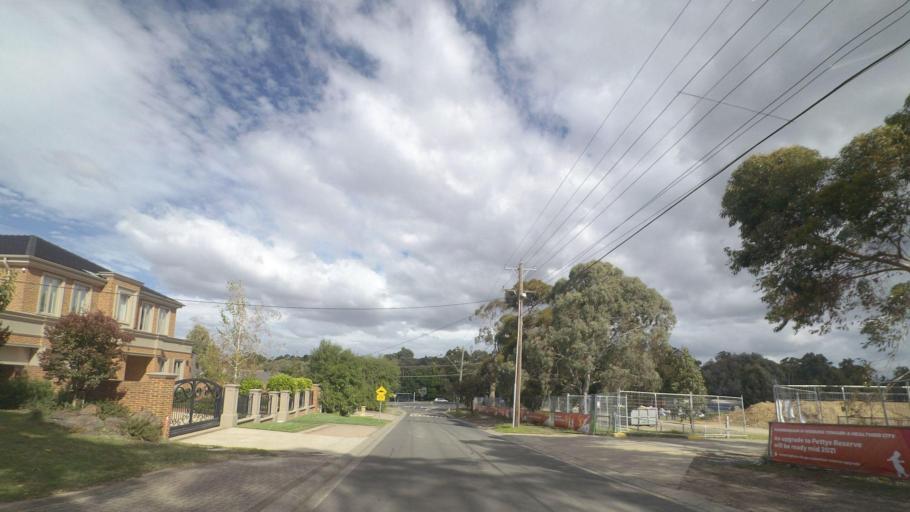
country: AU
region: Victoria
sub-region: Manningham
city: Doncaster East
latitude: -37.7610
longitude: 145.1532
